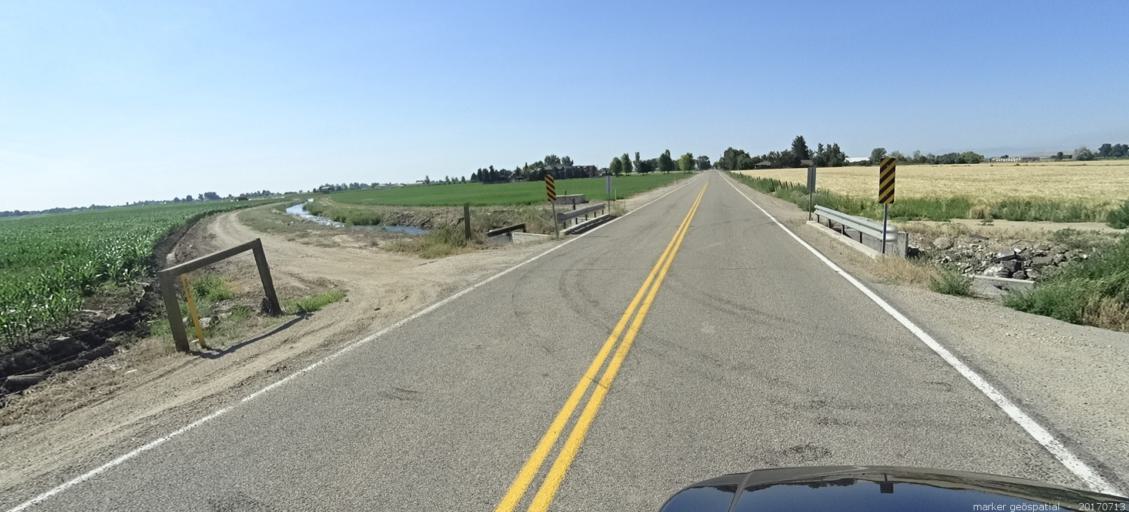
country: US
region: Idaho
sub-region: Ada County
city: Kuna
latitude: 43.5138
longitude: -116.3743
